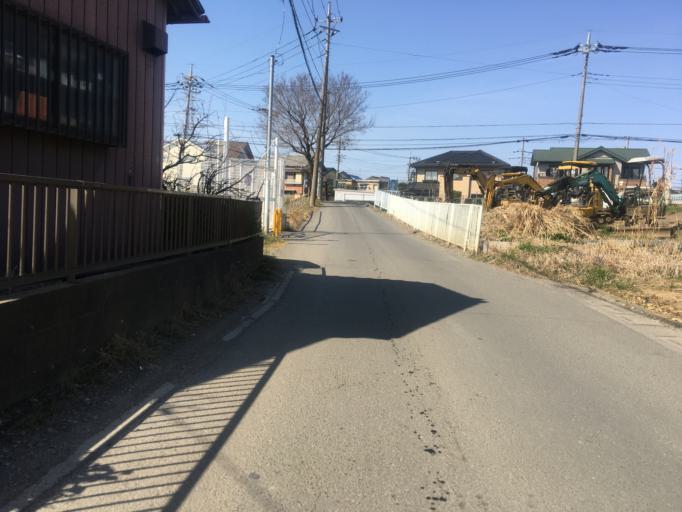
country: JP
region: Saitama
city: Shiki
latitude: 35.8304
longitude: 139.6010
